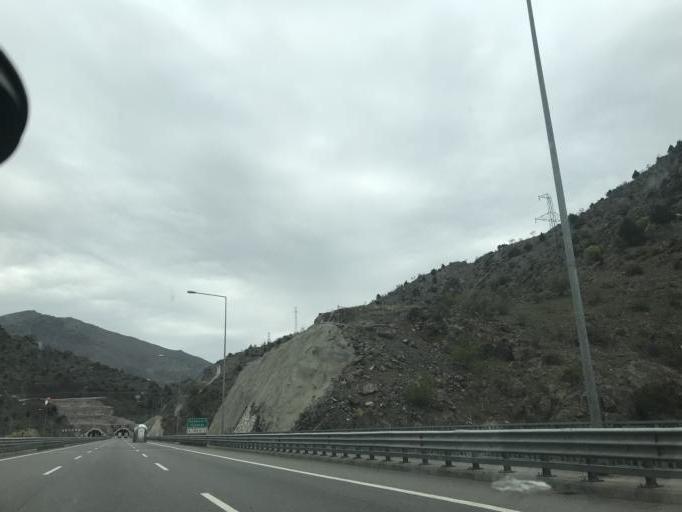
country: TR
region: Nigde
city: Ciftehan
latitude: 37.5543
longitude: 34.7721
